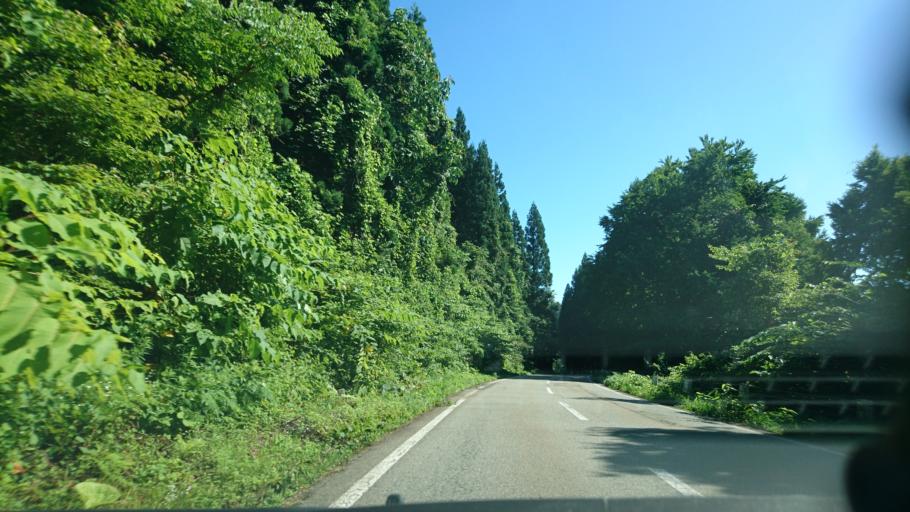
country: JP
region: Akita
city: Kakunodatemachi
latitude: 39.7451
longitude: 140.6374
